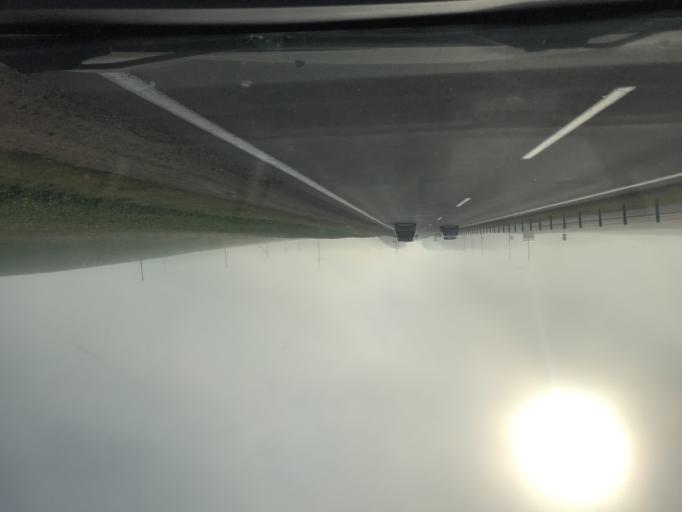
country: BY
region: Minsk
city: Luhavaya Slabada
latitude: 53.7255
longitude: 27.8579
